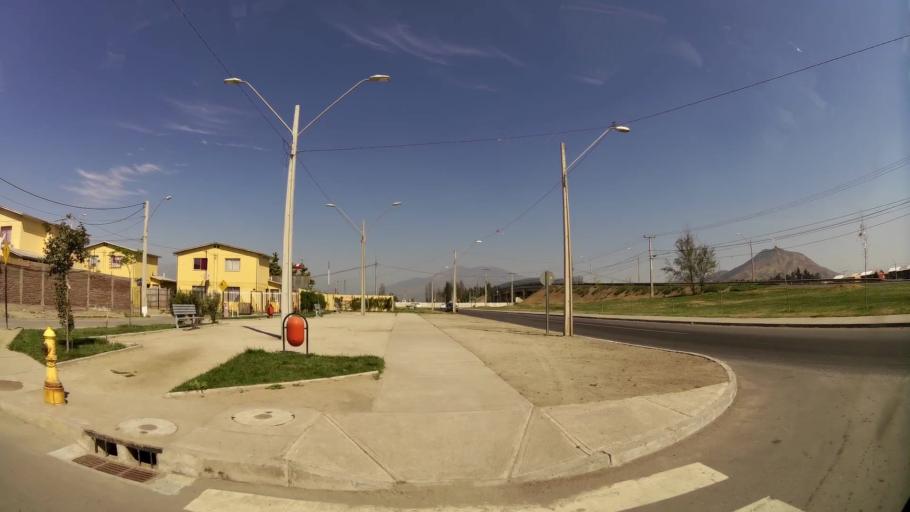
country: CL
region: Santiago Metropolitan
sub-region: Provincia de Cordillera
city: Puente Alto
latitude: -33.6310
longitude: -70.6113
